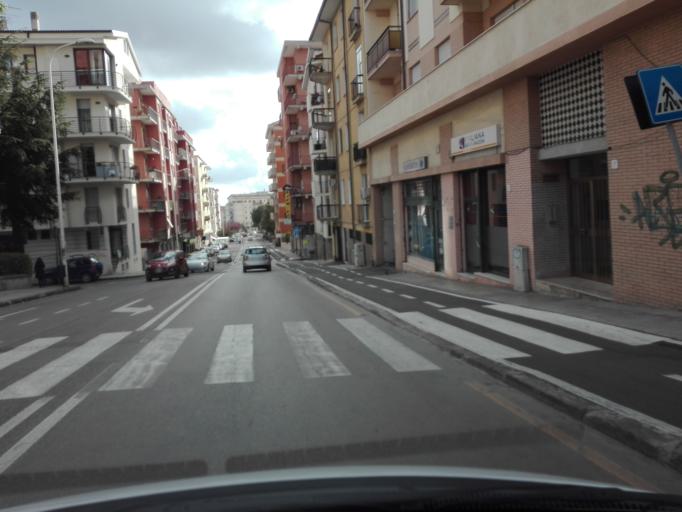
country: IT
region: Sardinia
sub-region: Provincia di Sassari
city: Sassari
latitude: 40.7166
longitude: 8.5686
